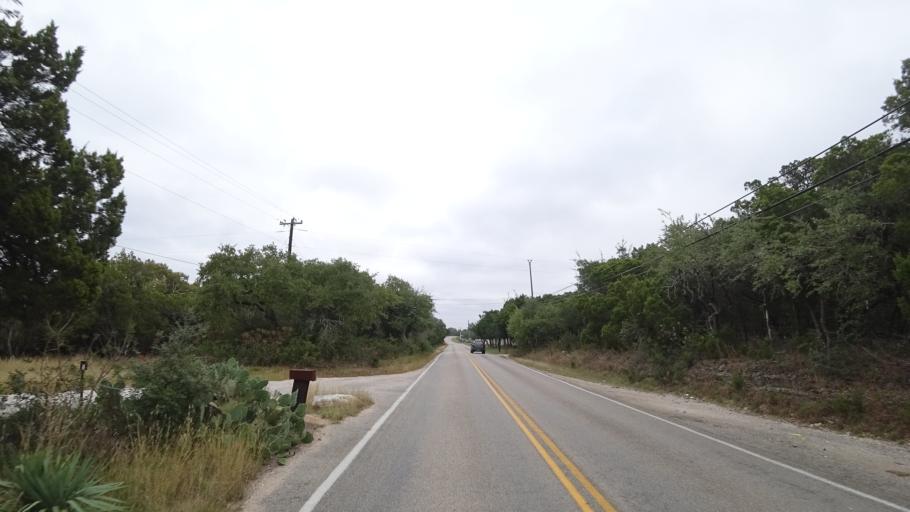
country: US
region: Texas
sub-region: Travis County
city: Barton Creek
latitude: 30.2559
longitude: -97.9154
